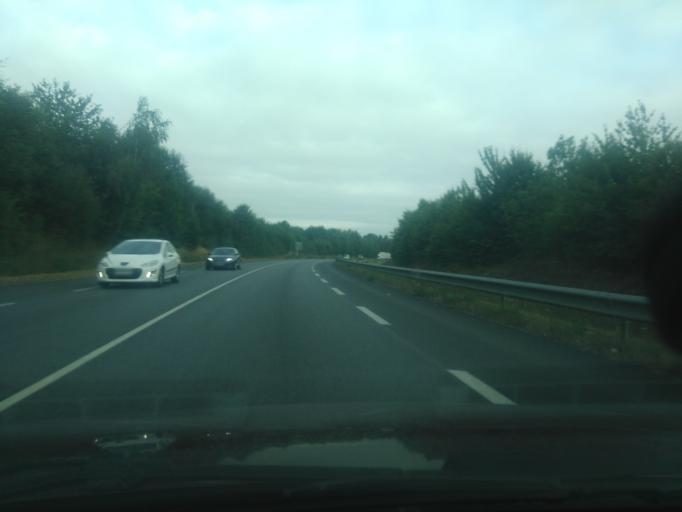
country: FR
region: Pays de la Loire
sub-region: Departement de la Vendee
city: La Roche-sur-Yon
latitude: 46.6782
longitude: -1.4033
